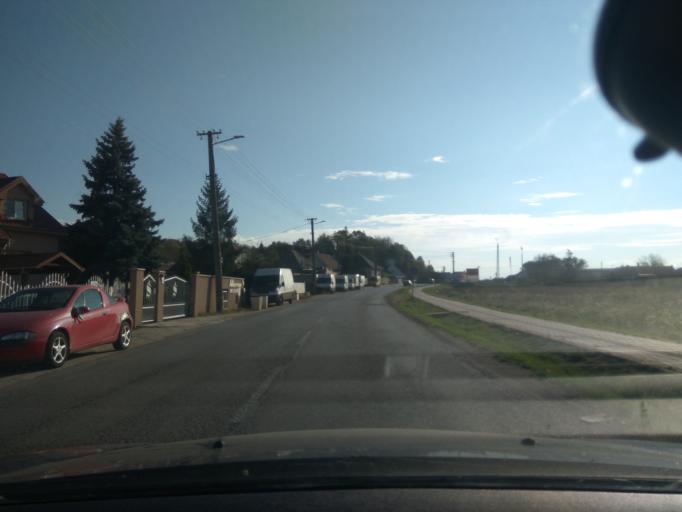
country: SK
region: Trnavsky
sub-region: Okres Trnava
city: Piestany
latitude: 48.5634
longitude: 17.8390
